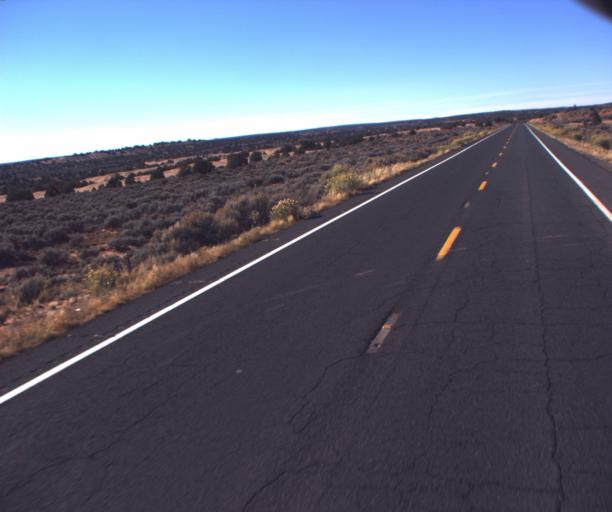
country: US
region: Arizona
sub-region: Coconino County
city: Kaibito
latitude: 36.5682
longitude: -110.7613
